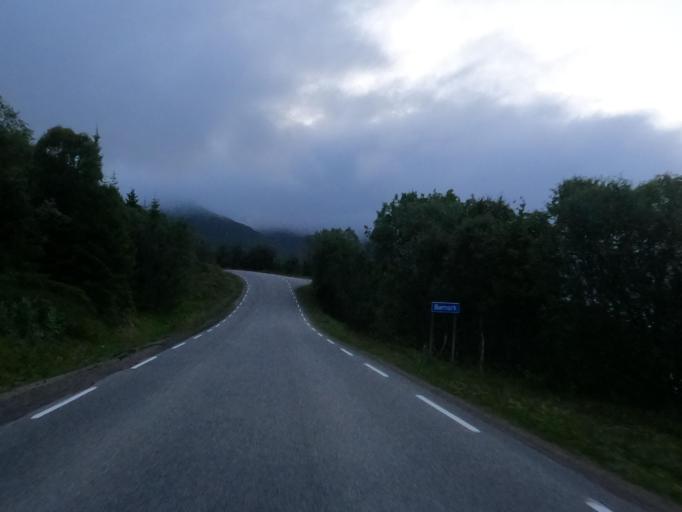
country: NO
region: Nordland
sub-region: Lodingen
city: Lodingen
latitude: 68.6012
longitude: 15.7882
